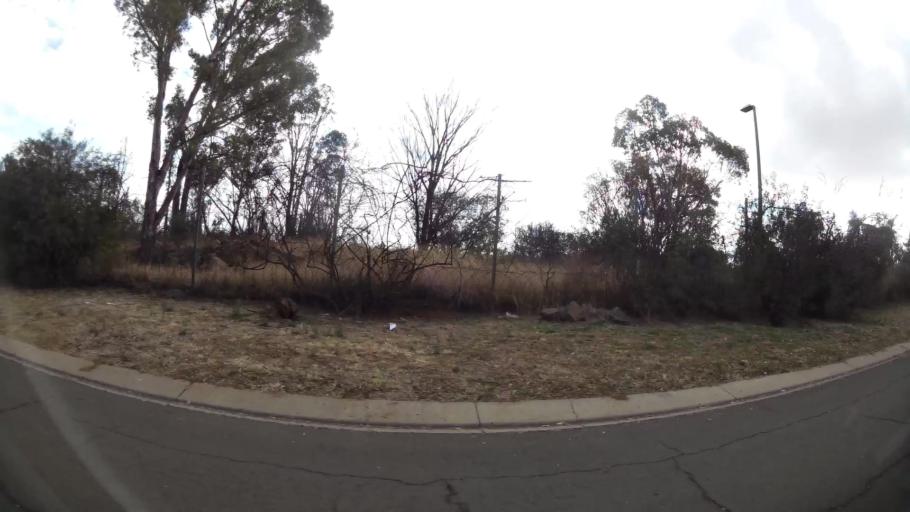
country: ZA
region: Orange Free State
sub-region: Mangaung Metropolitan Municipality
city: Bloemfontein
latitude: -29.0847
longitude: 26.1945
